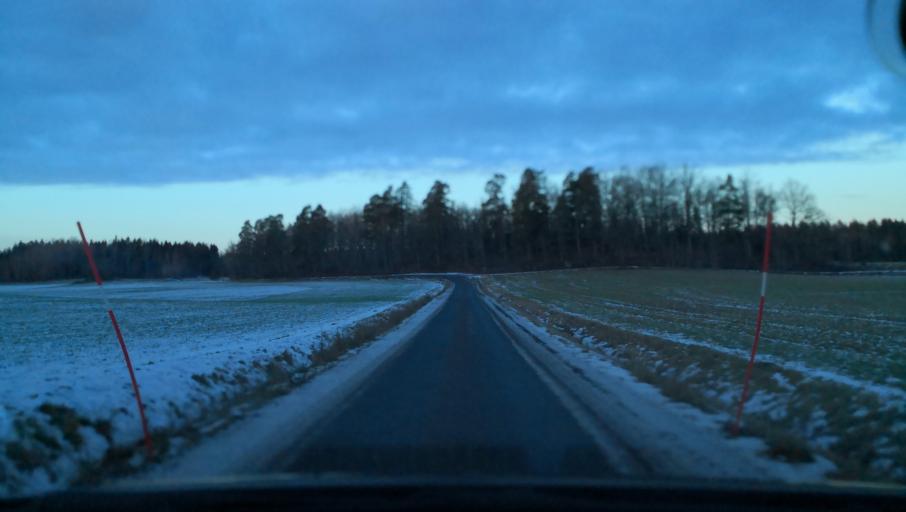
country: SE
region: Soedermanland
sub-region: Eskilstuna Kommun
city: Skogstorp
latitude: 59.2304
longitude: 16.3351
